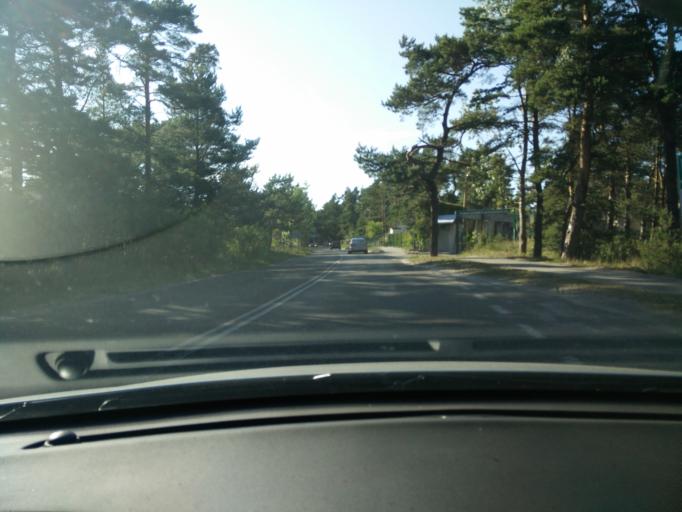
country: PL
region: Pomeranian Voivodeship
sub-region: Powiat pucki
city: Hel
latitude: 54.6198
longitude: 18.8009
